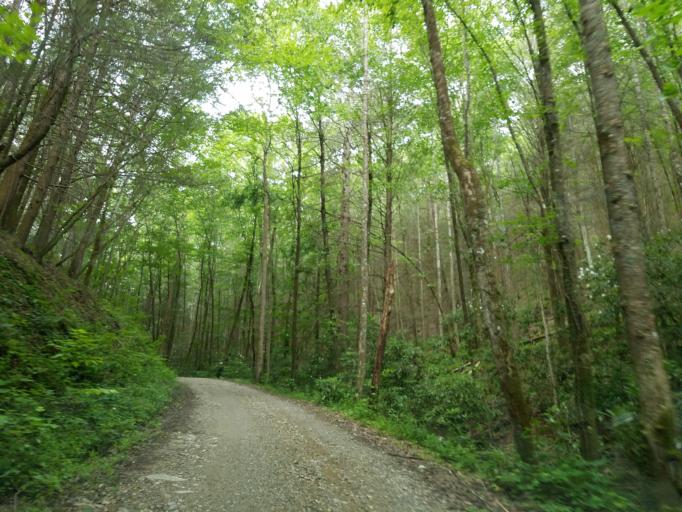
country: US
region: Georgia
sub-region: Union County
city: Blairsville
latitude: 34.7709
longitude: -84.0642
